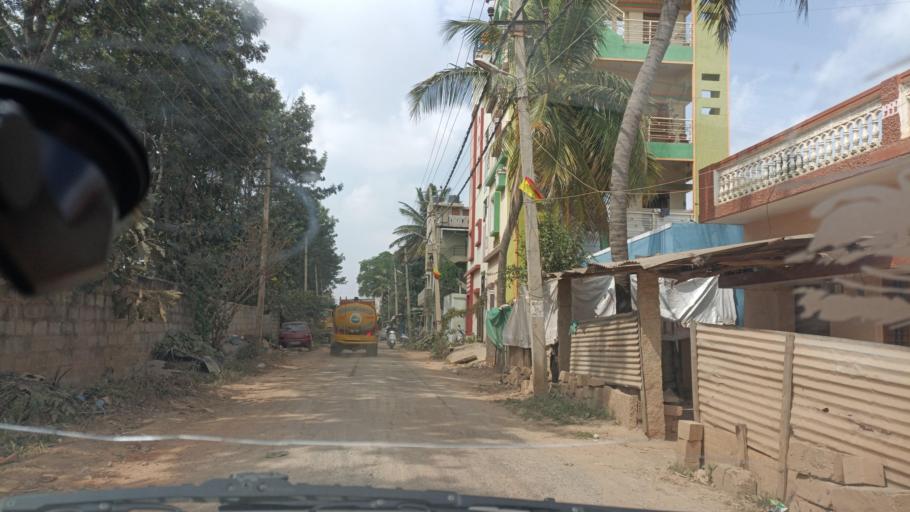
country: IN
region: Karnataka
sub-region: Bangalore Urban
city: Yelahanka
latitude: 13.1544
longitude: 77.6264
